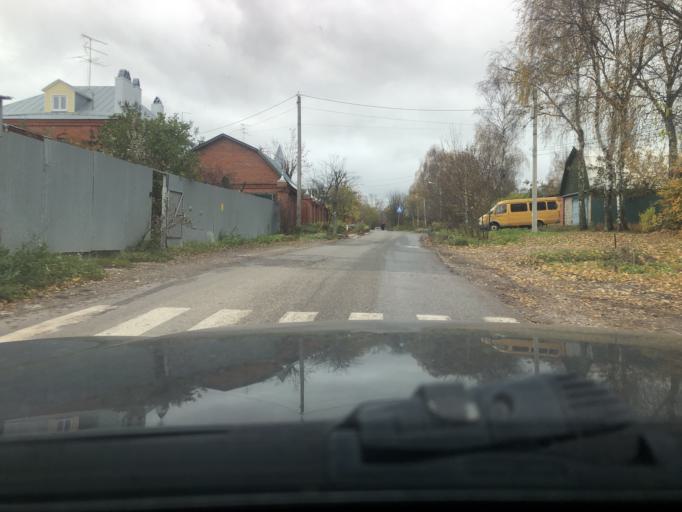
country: RU
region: Moskovskaya
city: Sergiyev Posad
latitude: 56.2984
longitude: 38.1121
